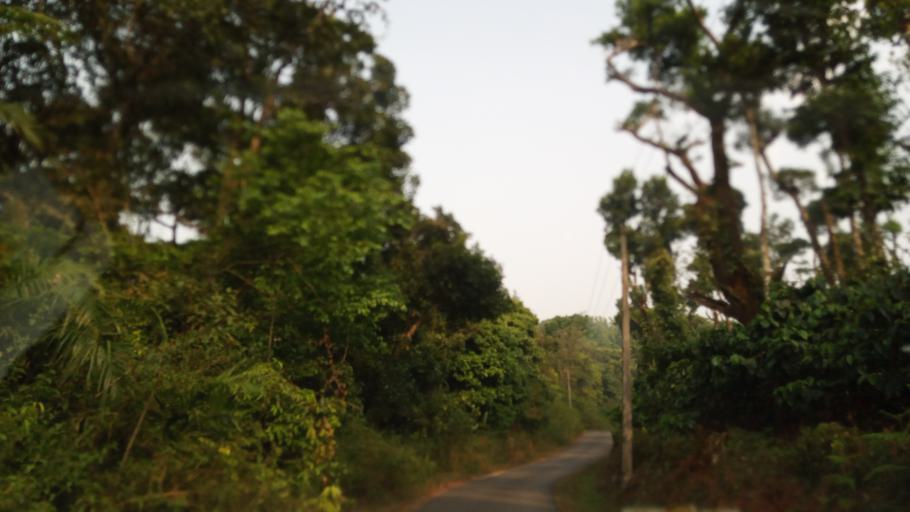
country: IN
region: Karnataka
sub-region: Chikmagalur
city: Mudigere
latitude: 13.0121
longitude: 75.6278
